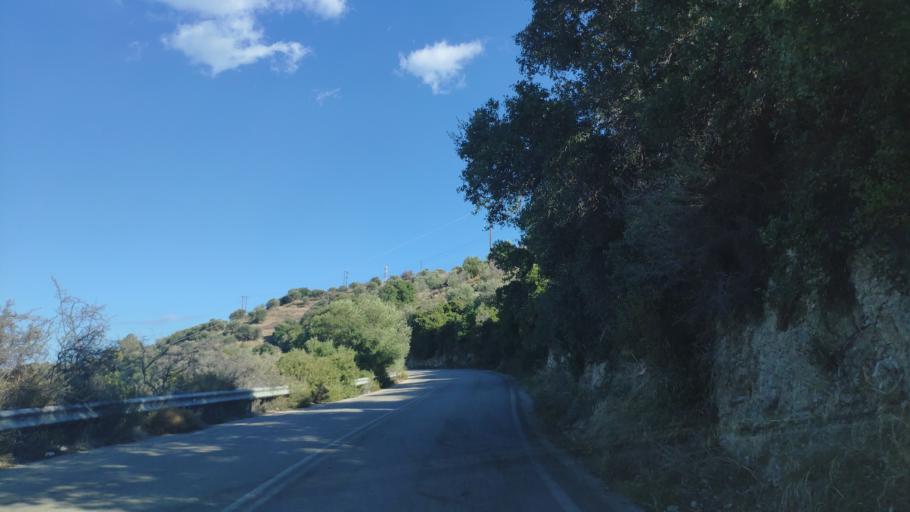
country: GR
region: Attica
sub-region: Nomos Piraios
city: Galatas
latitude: 37.5374
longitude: 23.3543
